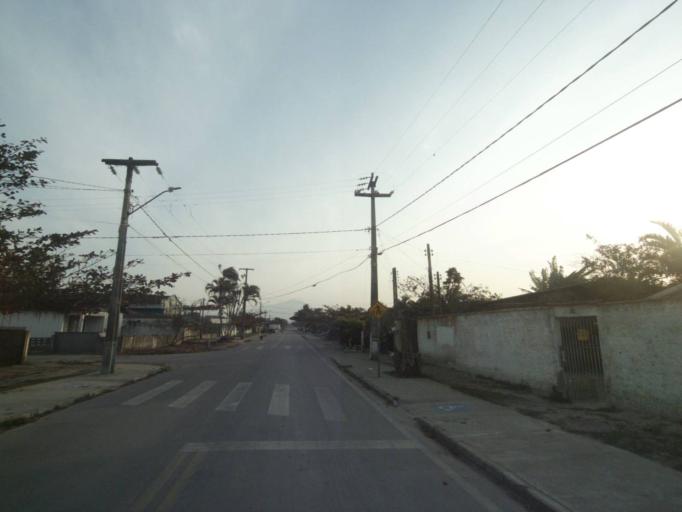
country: BR
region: Parana
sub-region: Paranagua
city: Paranagua
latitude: -25.5129
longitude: -48.5382
